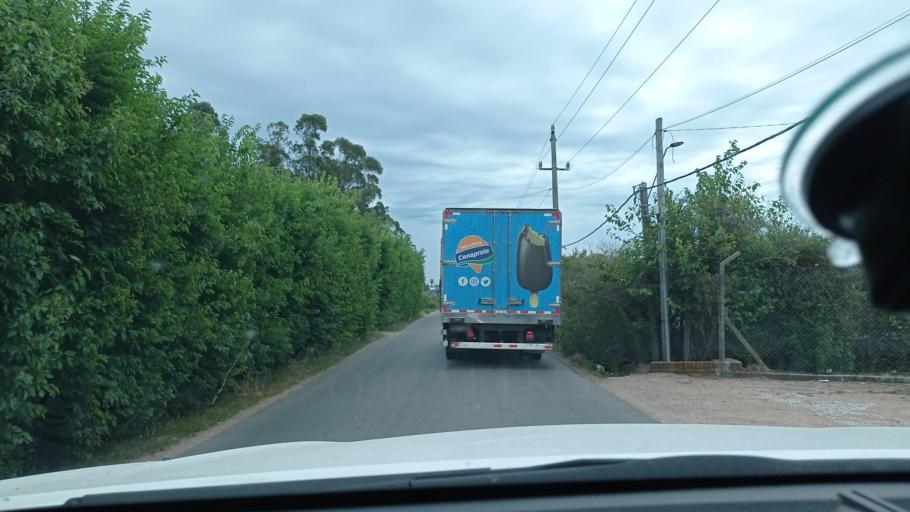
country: UY
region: Canelones
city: La Paz
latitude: -34.8068
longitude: -56.1887
